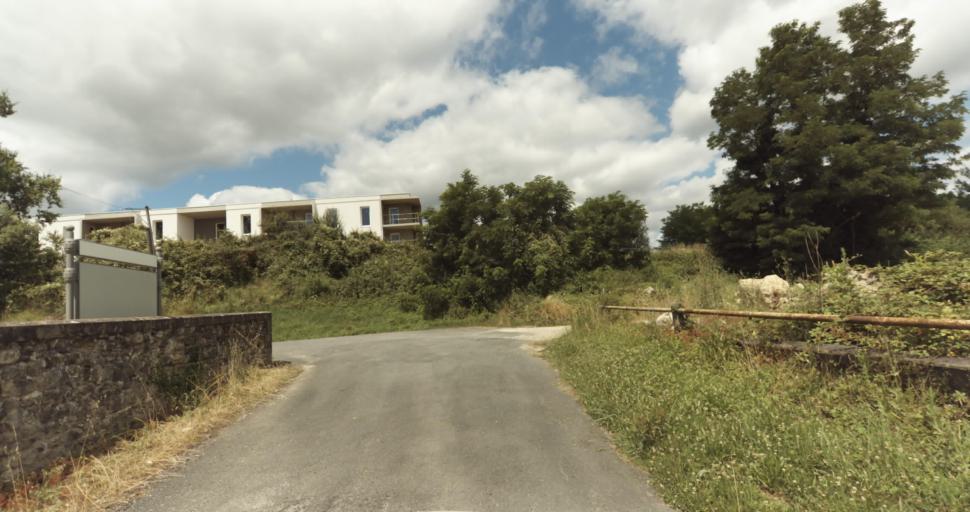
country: FR
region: Aquitaine
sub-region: Departement de la Gironde
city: Bazas
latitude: 44.4361
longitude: -0.2157
